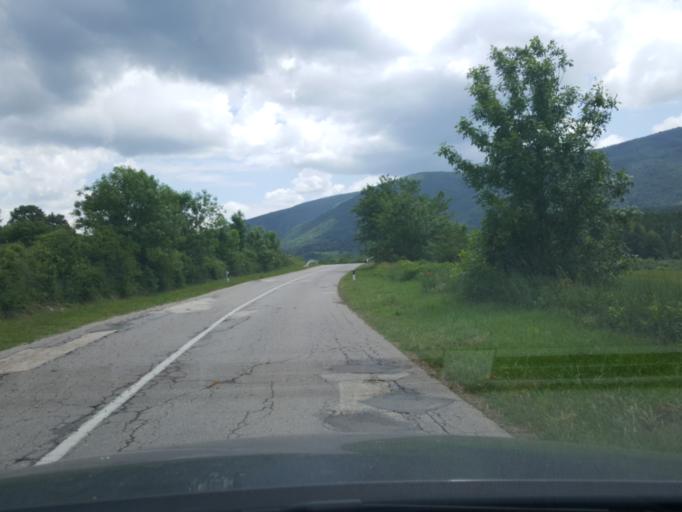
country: RS
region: Central Serbia
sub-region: Zajecarski Okrug
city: Soko Banja
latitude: 43.6414
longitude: 21.9532
